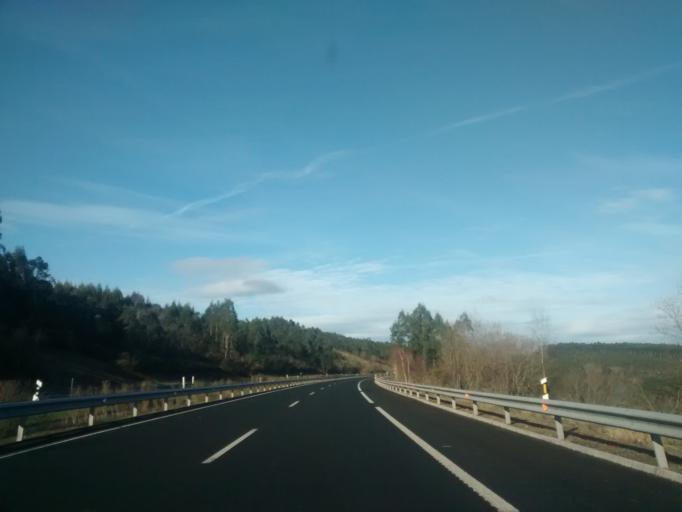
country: ES
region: Cantabria
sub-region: Provincia de Cantabria
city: Cabezon de la Sal
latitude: 43.3232
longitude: -4.2913
